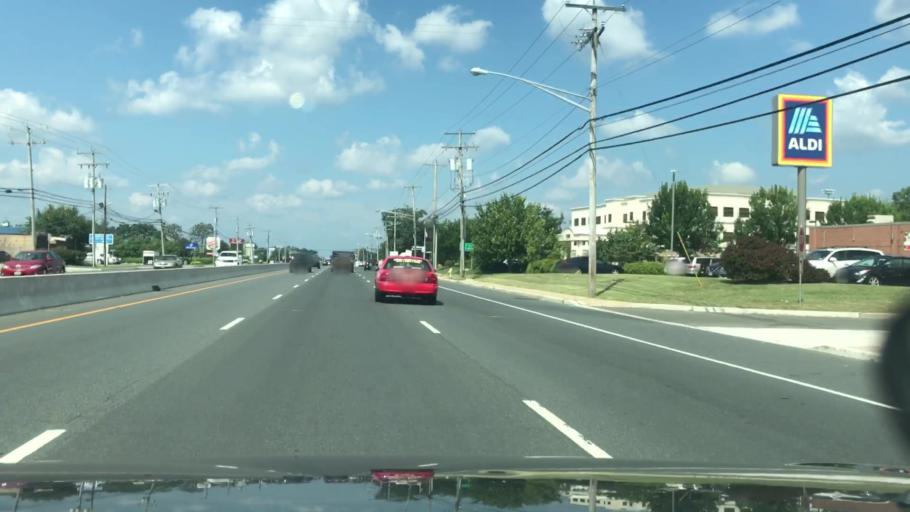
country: US
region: New Jersey
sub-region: Ocean County
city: Holiday City South
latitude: 39.9700
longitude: -74.2335
